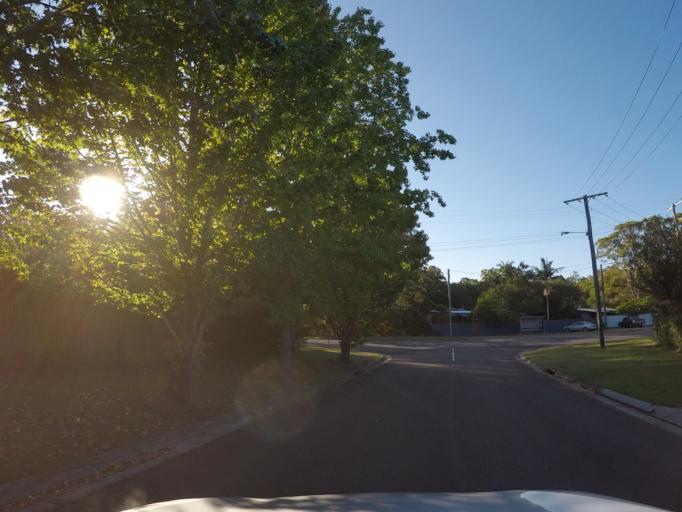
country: AU
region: Queensland
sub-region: Sunshine Coast
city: Nambour
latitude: -26.6279
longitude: 152.8614
